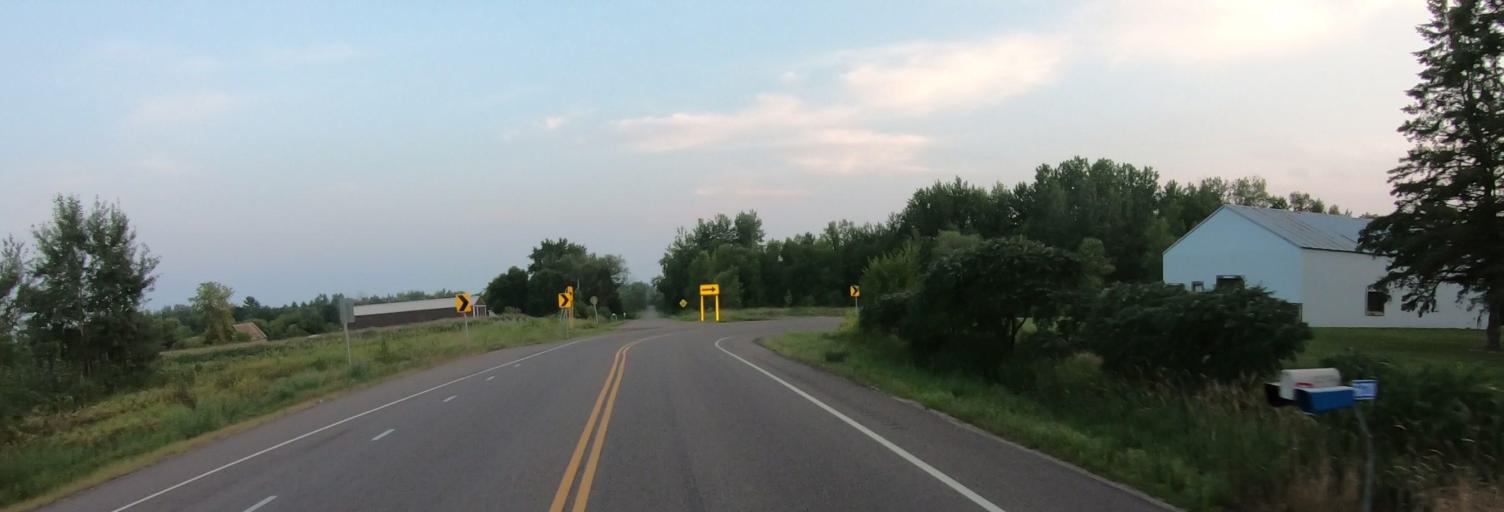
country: US
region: Minnesota
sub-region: Pine County
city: Rock Creek
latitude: 45.7670
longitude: -92.9602
